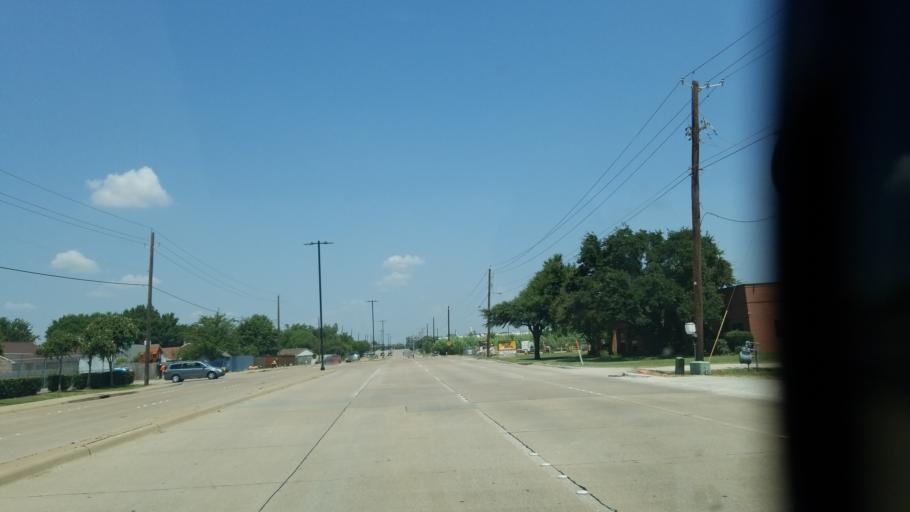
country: US
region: Texas
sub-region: Dallas County
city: Garland
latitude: 32.9260
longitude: -96.6307
